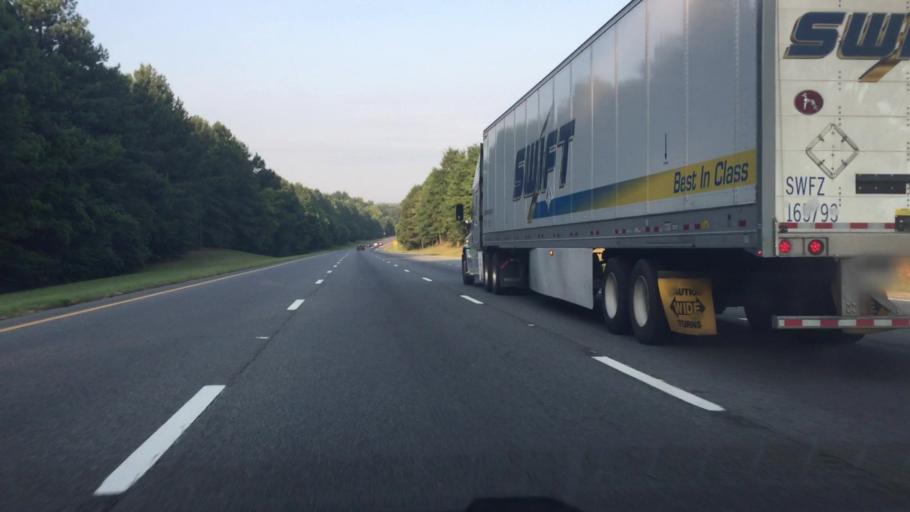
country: US
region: North Carolina
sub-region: Davidson County
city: Lexington
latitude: 35.7929
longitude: -80.2217
